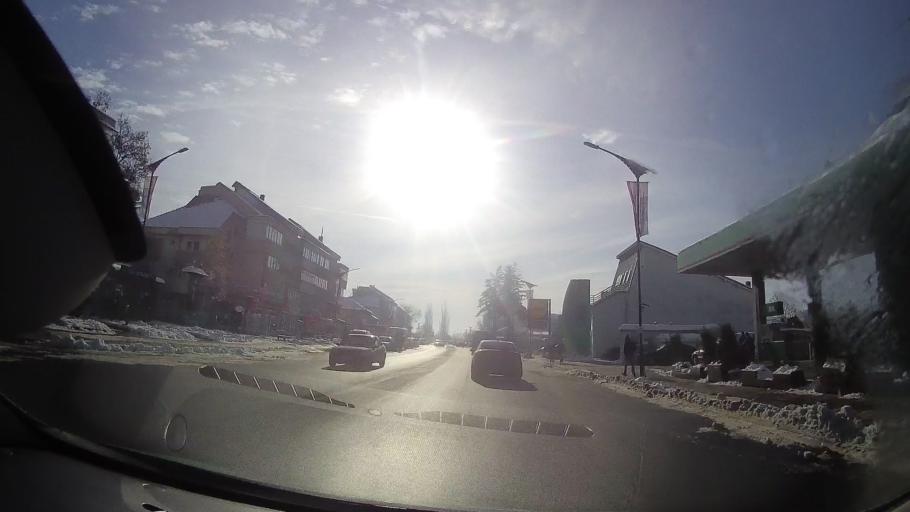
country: RO
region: Neamt
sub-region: Oras Targu Neamt
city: Humulesti
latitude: 47.2041
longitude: 26.3585
